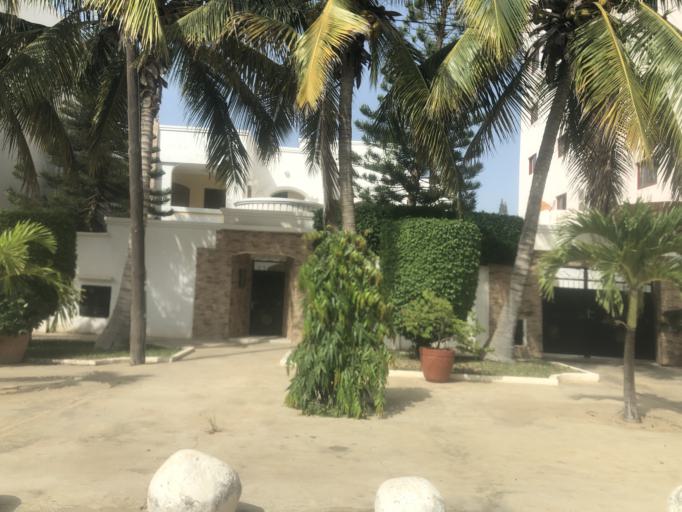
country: SN
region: Dakar
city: Mermoz Boabab
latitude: 14.7394
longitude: -17.5146
